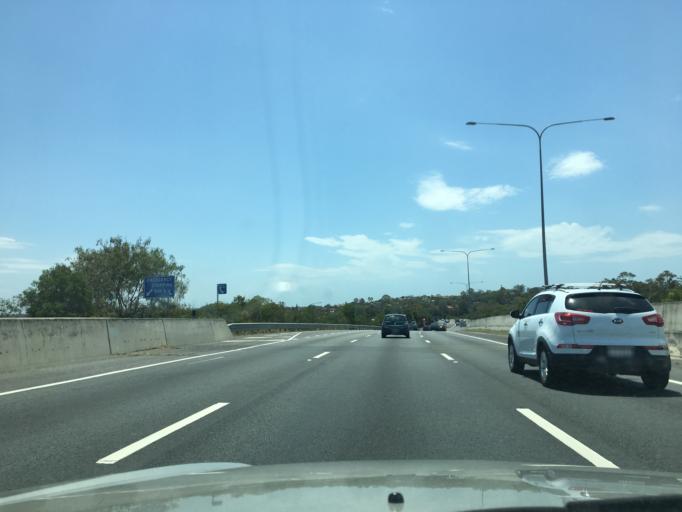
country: AU
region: Queensland
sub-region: Brisbane
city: Belmont
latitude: -27.5029
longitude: 153.1245
